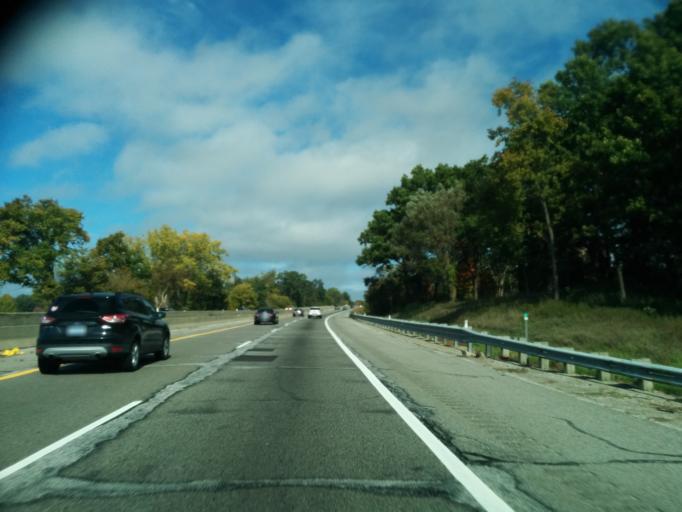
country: US
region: Michigan
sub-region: Livingston County
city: Brighton
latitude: 42.6595
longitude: -83.7587
